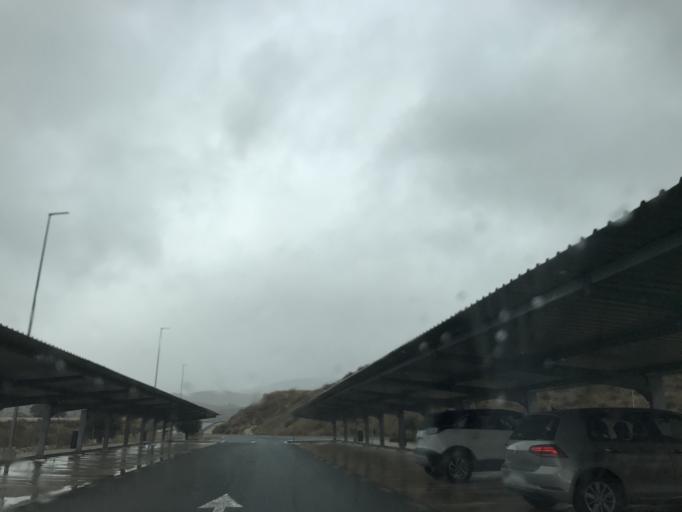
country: ES
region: Andalusia
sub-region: Provincia de Malaga
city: Casabermeja
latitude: 36.9171
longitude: -4.4392
